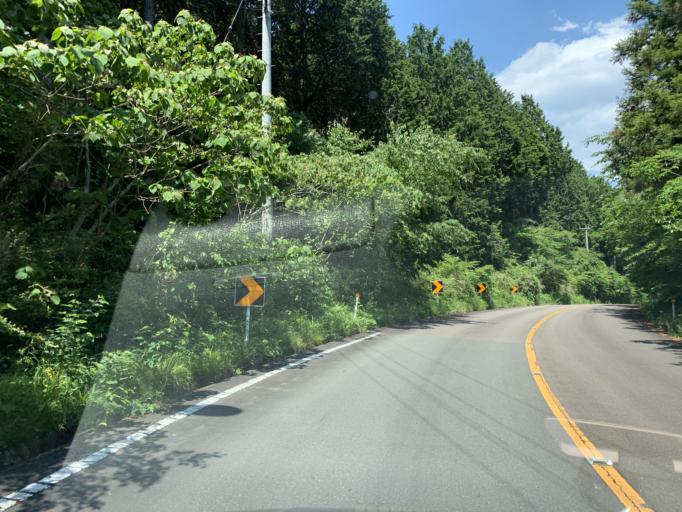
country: JP
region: Miyagi
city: Matsushima
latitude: 38.3644
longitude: 141.0474
